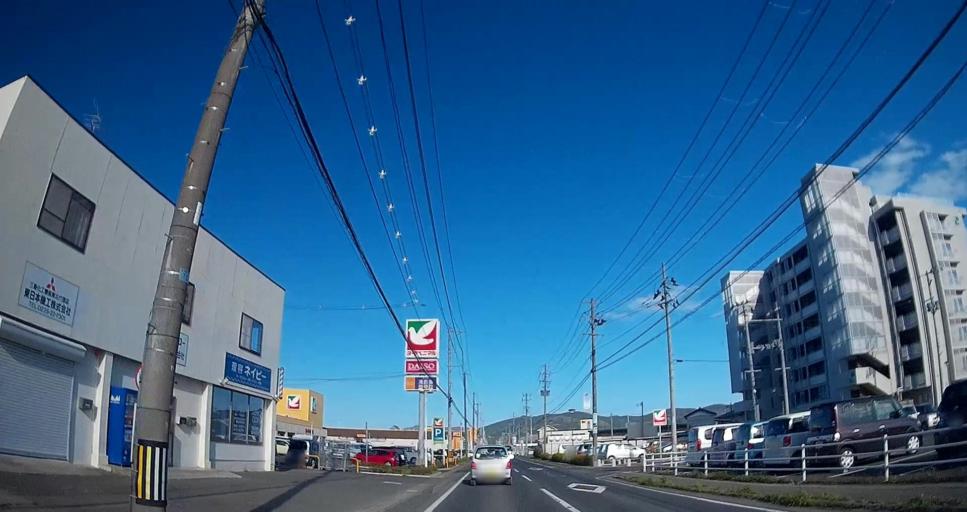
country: JP
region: Miyagi
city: Ishinomaki
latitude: 38.4188
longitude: 141.3374
